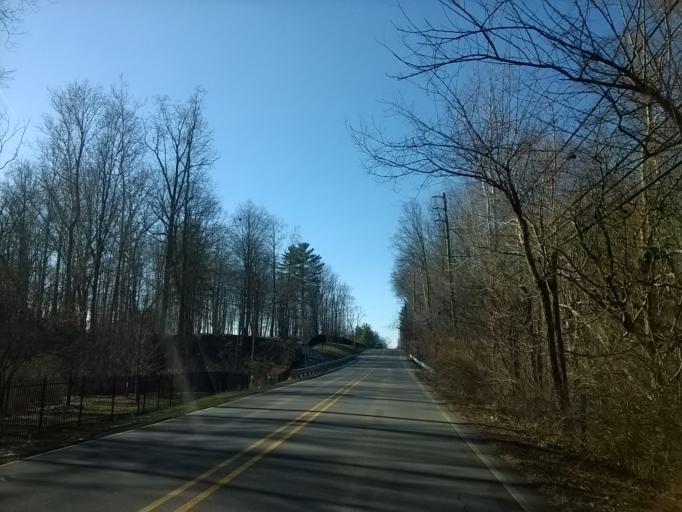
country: US
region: Indiana
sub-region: Marion County
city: Meridian Hills
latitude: 39.9416
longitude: -86.1669
